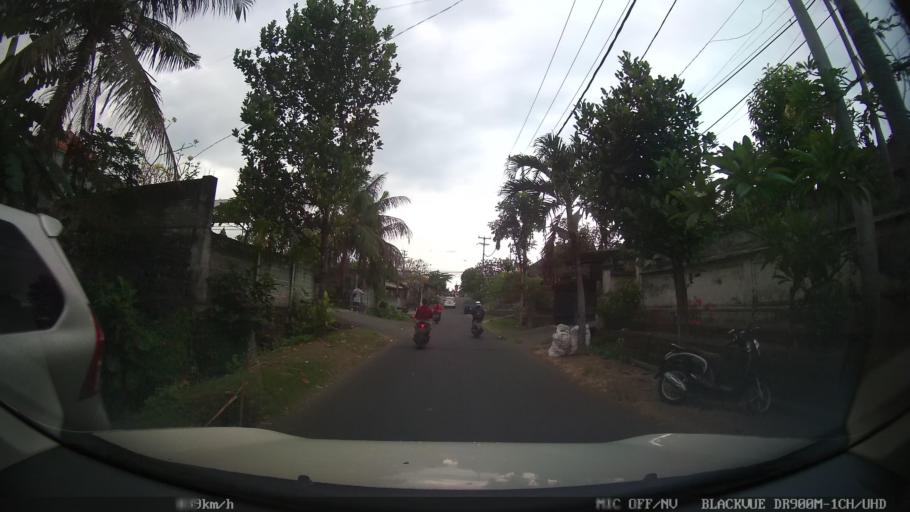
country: ID
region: Bali
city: Banjar Pasekan
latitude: -8.6278
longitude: 115.2933
